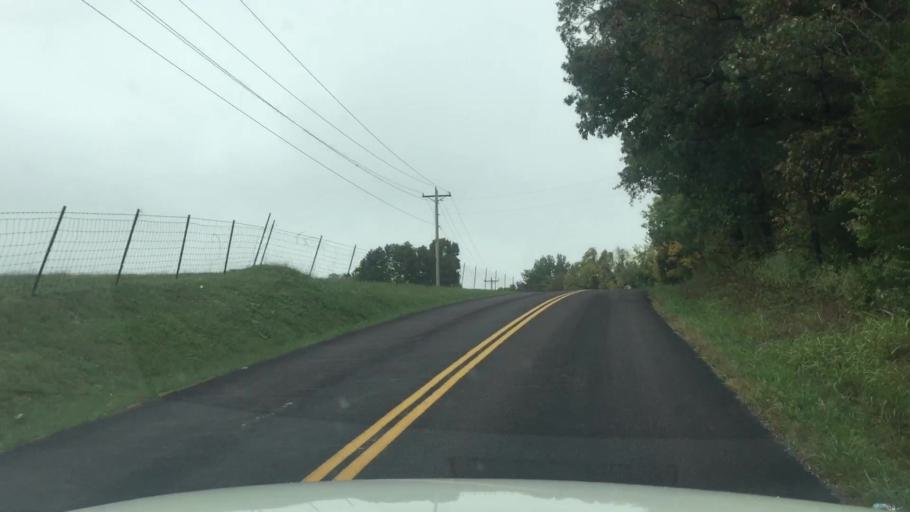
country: US
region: Missouri
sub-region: Boone County
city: Ashland
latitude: 38.8219
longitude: -92.3481
